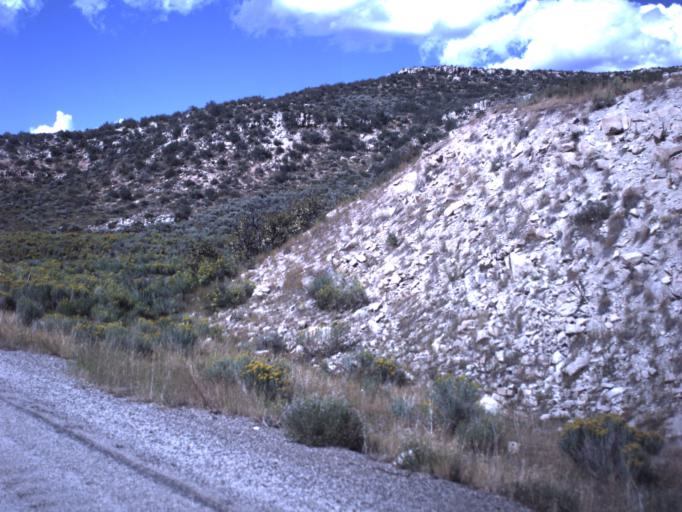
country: US
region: Utah
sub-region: Summit County
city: Francis
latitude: 40.2000
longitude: -110.9684
